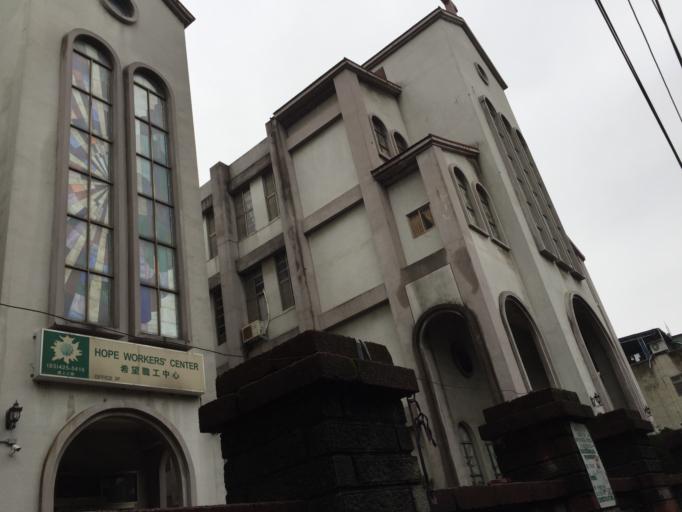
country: TW
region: Taiwan
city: Taoyuan City
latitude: 24.9566
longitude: 121.2282
